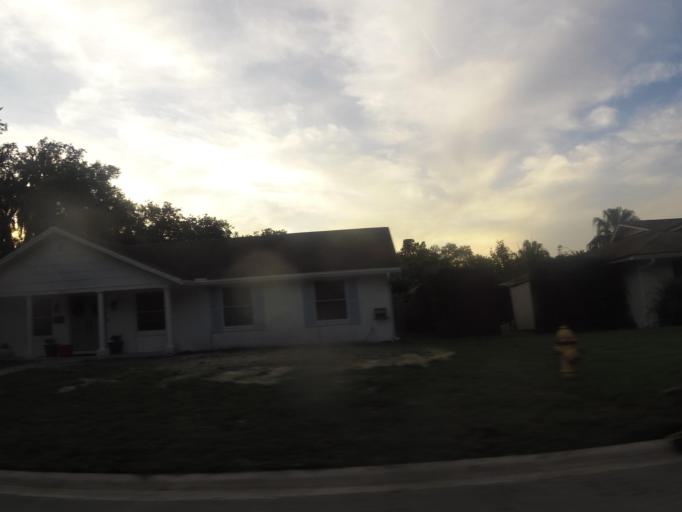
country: US
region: Florida
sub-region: Duval County
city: Jacksonville
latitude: 30.2767
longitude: -81.6588
